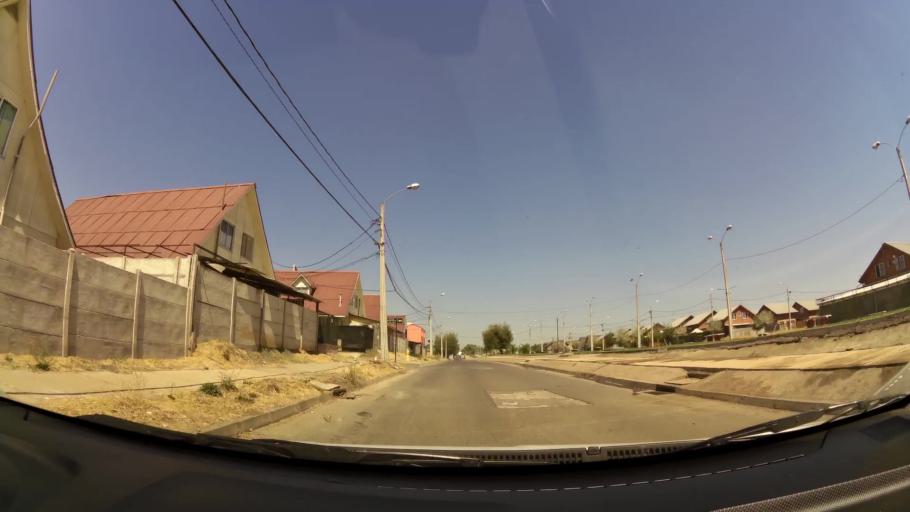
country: CL
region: Maule
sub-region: Provincia de Talca
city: Talca
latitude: -35.4013
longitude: -71.6447
